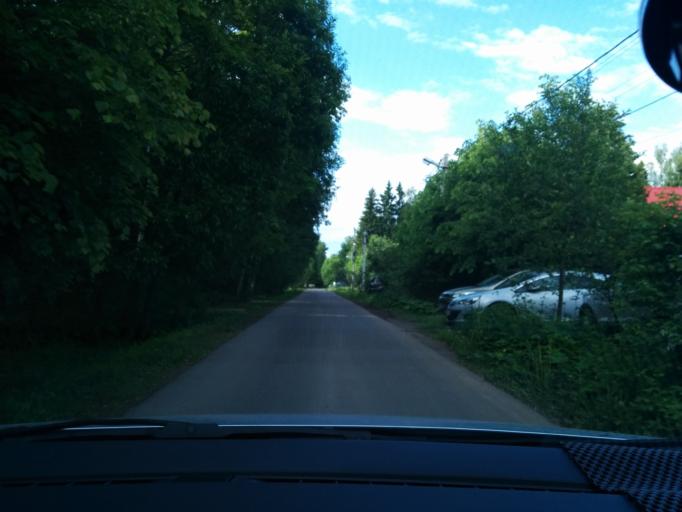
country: RU
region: Moskovskaya
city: Lugovaya
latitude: 56.0558
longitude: 37.4783
